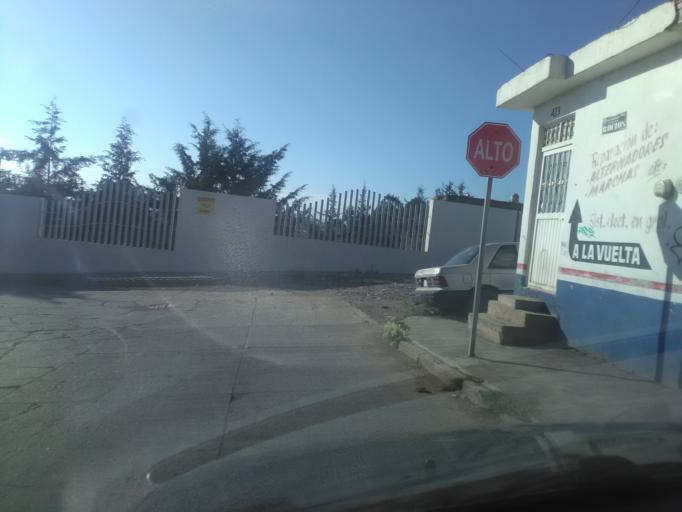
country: MX
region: Durango
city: Victoria de Durango
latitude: 24.0444
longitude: -104.6957
